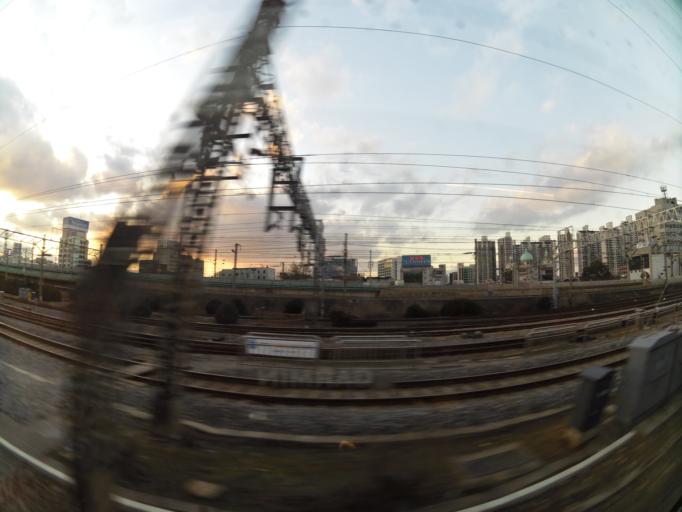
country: KR
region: Gyeonggi-do
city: Kwangmyong
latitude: 37.5013
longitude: 126.8806
